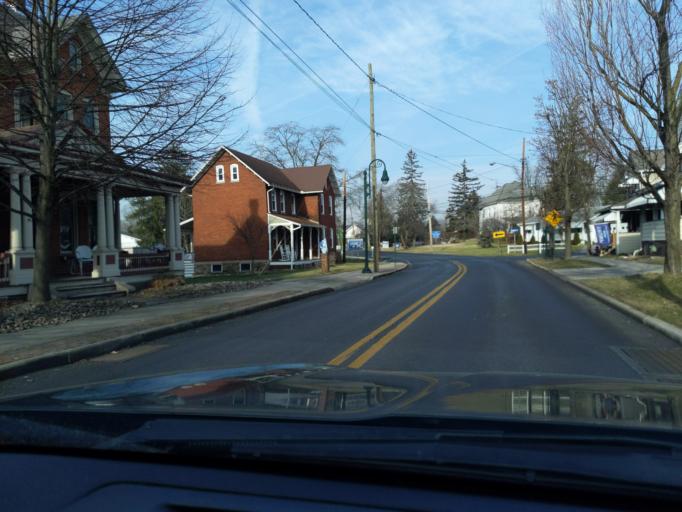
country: US
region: Pennsylvania
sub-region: Blair County
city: Hollidaysburg
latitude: 40.4319
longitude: -78.3998
